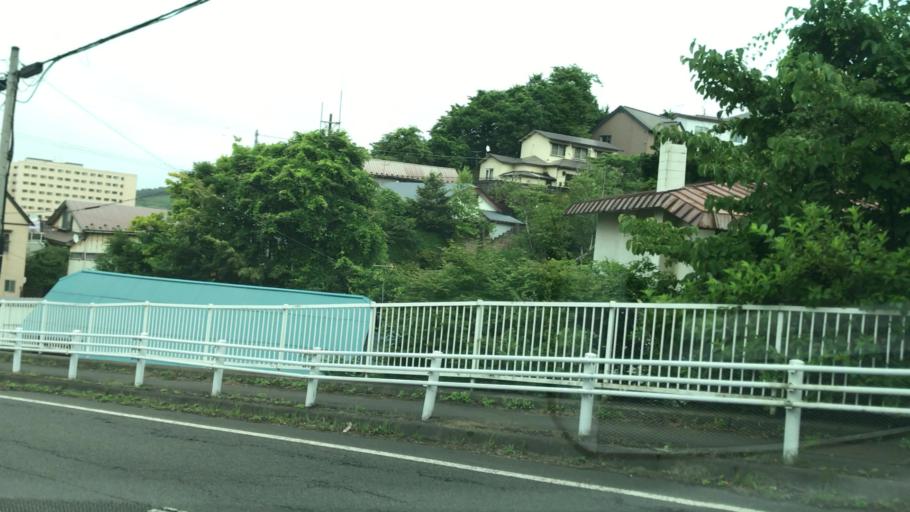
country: JP
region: Hokkaido
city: Muroran
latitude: 42.3315
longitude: 141.0065
